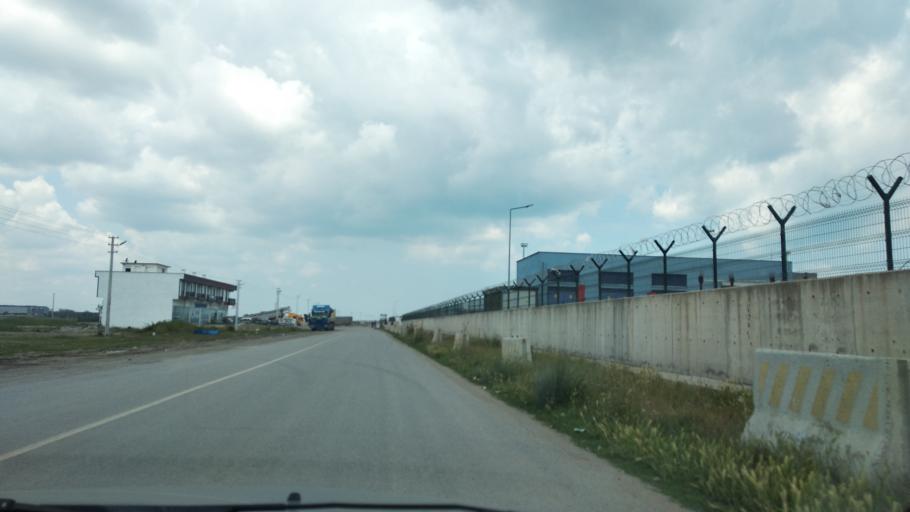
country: TR
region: Sakarya
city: Karasu
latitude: 41.1179
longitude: 30.6720
